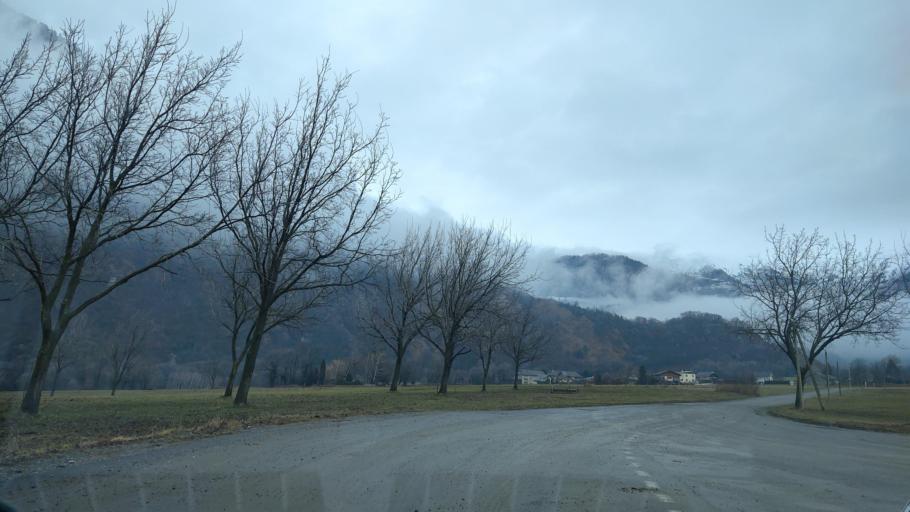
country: FR
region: Rhone-Alpes
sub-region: Departement de la Savoie
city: La Chambre
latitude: 45.3649
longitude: 6.2911
